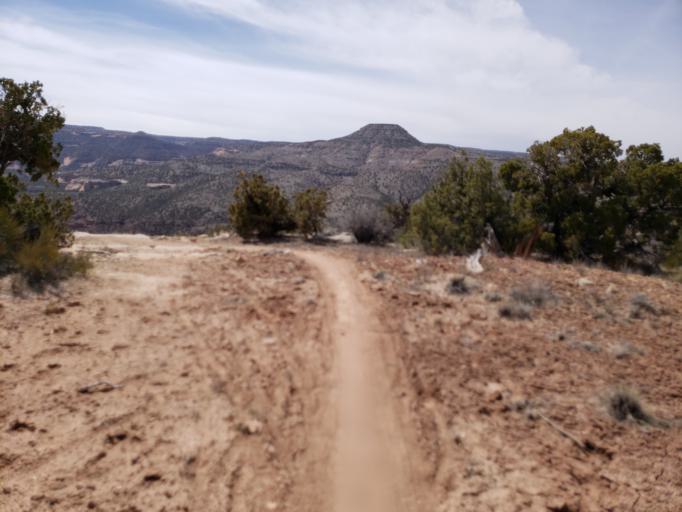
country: US
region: Colorado
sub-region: Mesa County
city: Loma
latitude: 39.1851
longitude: -108.8699
